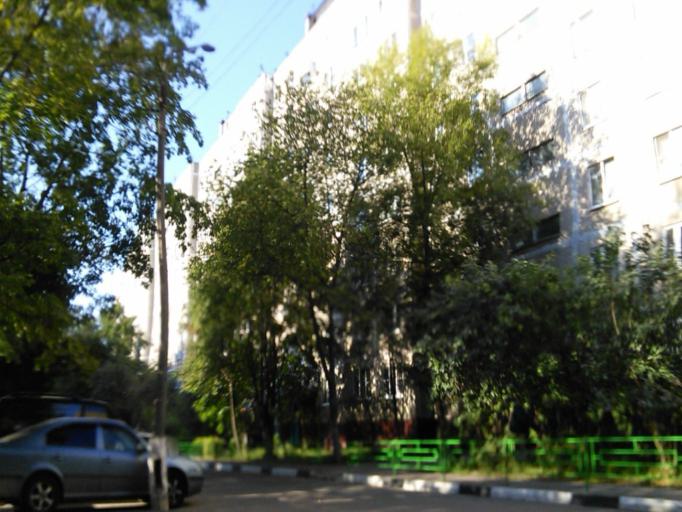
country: RU
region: Moskovskaya
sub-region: Podol'skiy Rayon
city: Podol'sk
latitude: 55.4421
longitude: 37.5657
